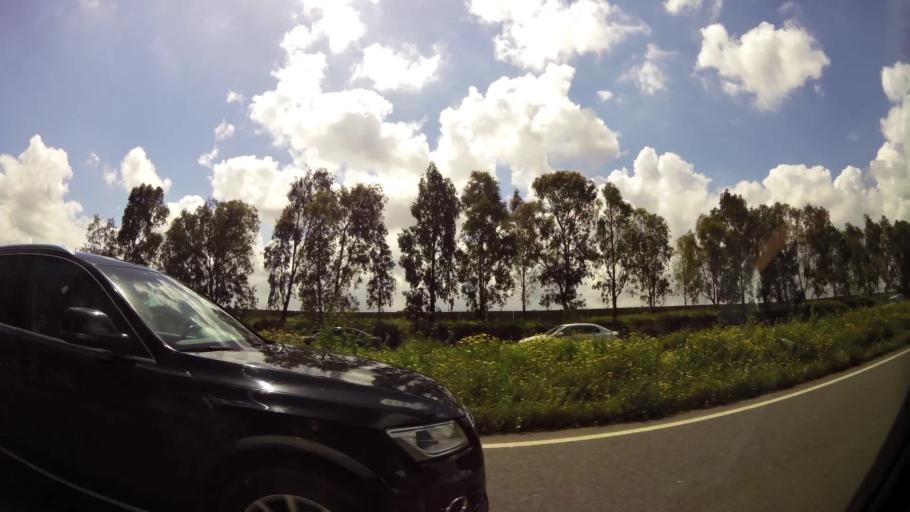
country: MA
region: Grand Casablanca
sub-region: Mediouna
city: Tit Mellil
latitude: 33.5575
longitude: -7.5081
